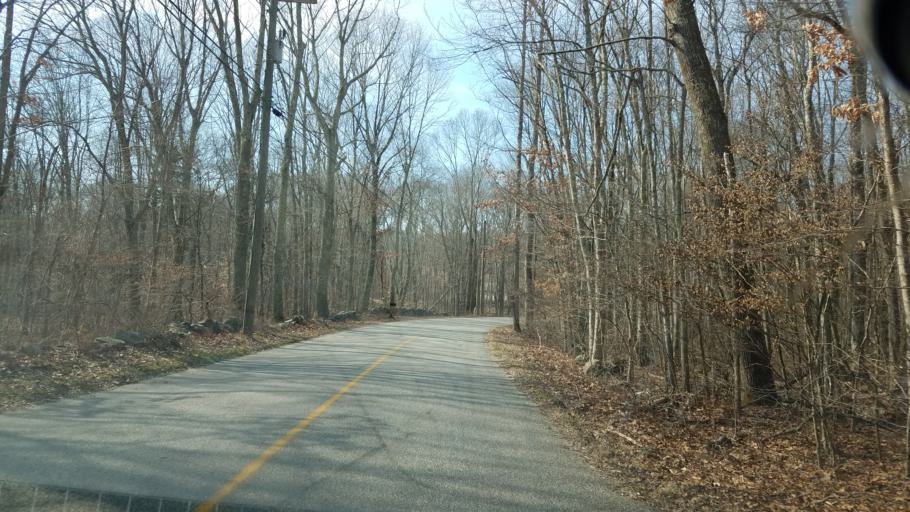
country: US
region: Connecticut
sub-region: New London County
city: Preston City
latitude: 41.5038
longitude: -71.9926
